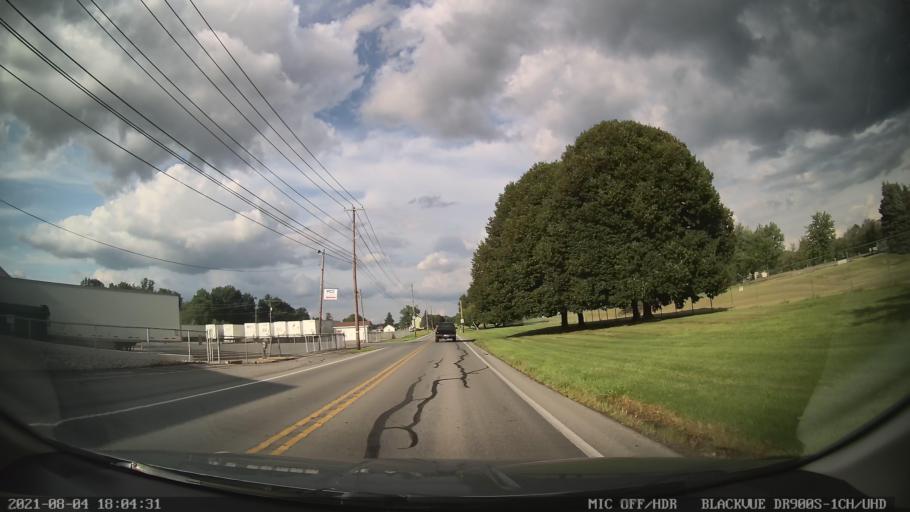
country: US
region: Pennsylvania
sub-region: Lehigh County
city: Trexlertown
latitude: 40.5572
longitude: -75.6025
